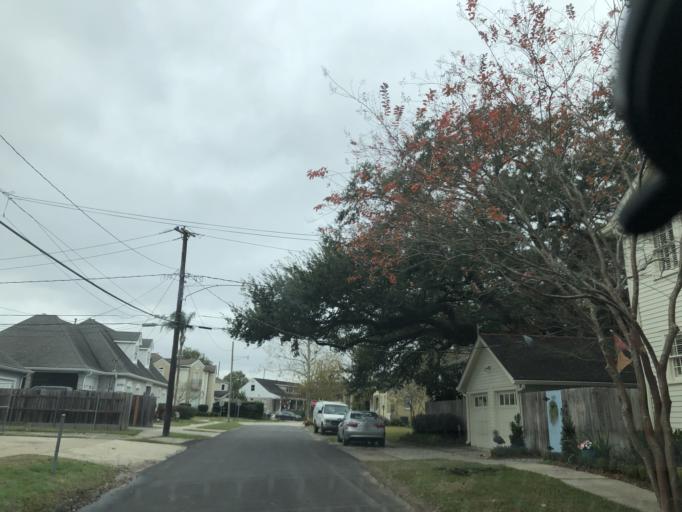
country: US
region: Louisiana
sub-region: Jefferson Parish
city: Metairie
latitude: 29.9812
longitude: -90.1492
